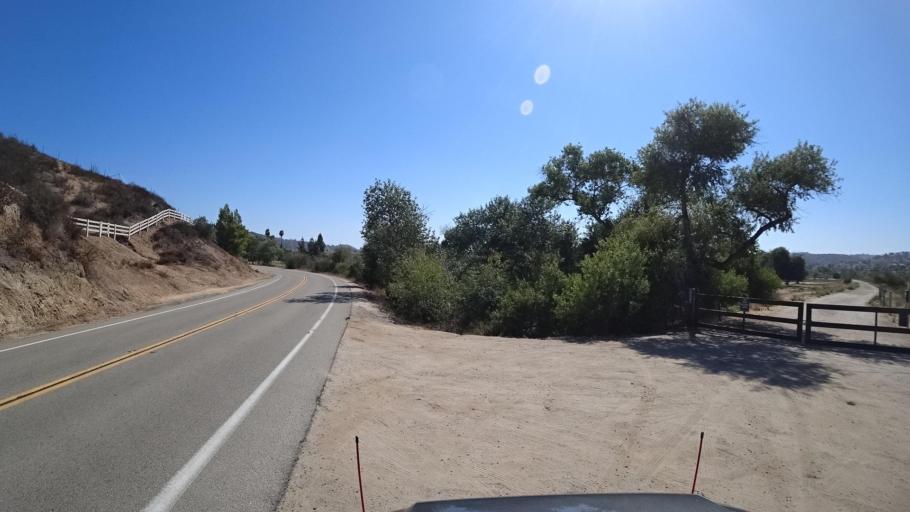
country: US
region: California
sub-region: San Diego County
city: Bonsall
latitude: 33.2929
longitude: -117.2168
